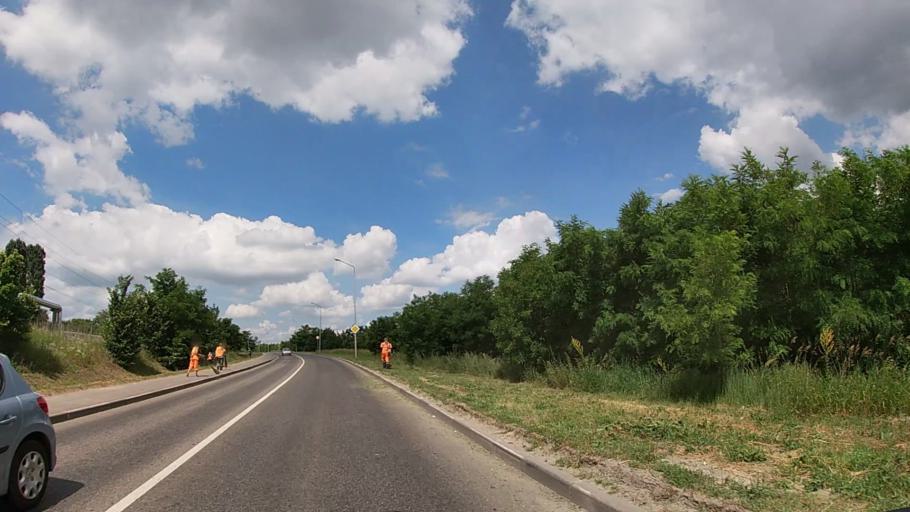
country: RU
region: Belgorod
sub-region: Belgorodskiy Rayon
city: Belgorod
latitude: 50.5934
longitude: 36.5596
